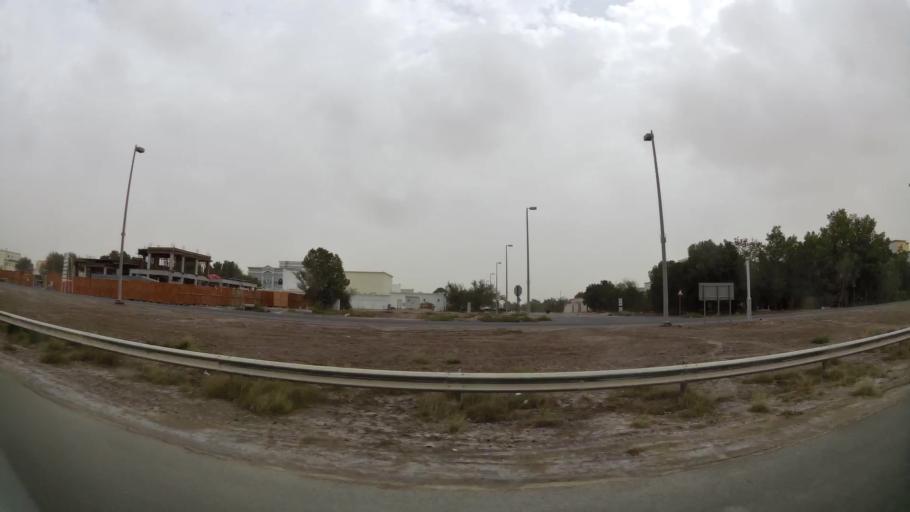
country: AE
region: Abu Dhabi
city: Abu Dhabi
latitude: 24.4077
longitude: 54.7337
